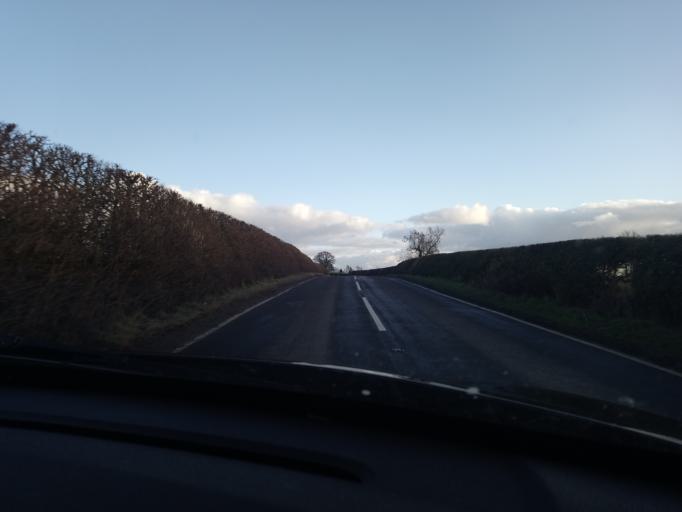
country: GB
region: England
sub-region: Shropshire
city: Wem
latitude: 52.8623
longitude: -2.7551
